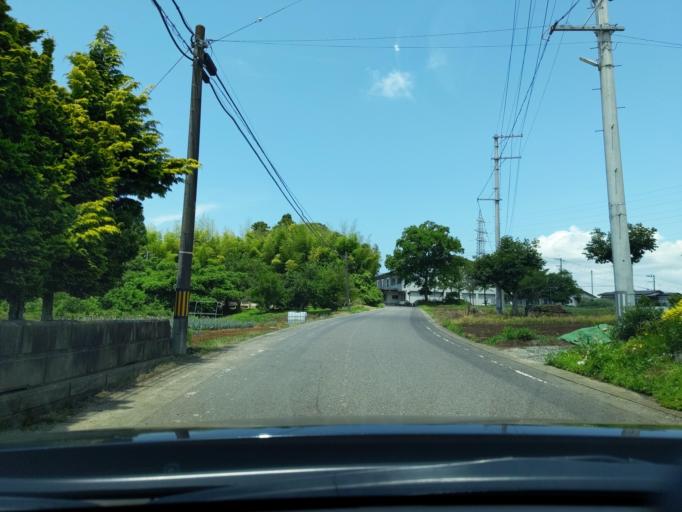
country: JP
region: Fukushima
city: Sukagawa
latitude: 37.3357
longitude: 140.3522
